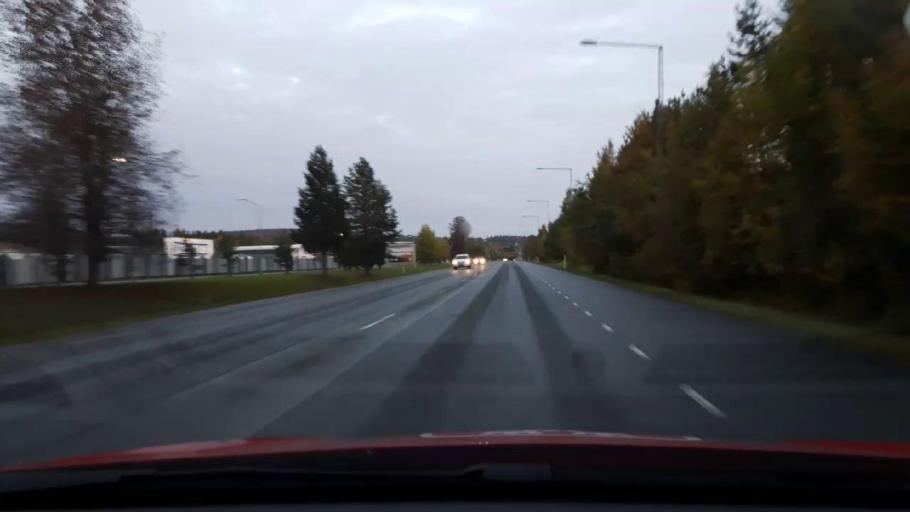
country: SE
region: Jaemtland
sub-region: OEstersunds Kommun
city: Ostersund
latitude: 63.2089
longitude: 14.6379
